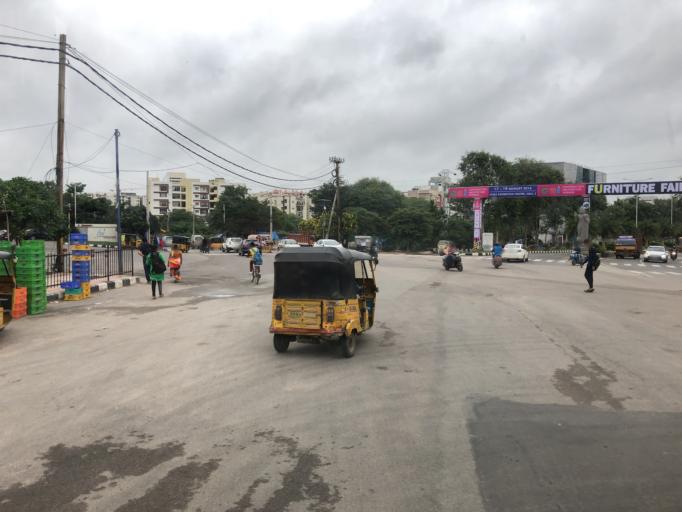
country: IN
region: Telangana
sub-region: Rangareddi
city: Kukatpalli
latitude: 17.4639
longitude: 78.3759
